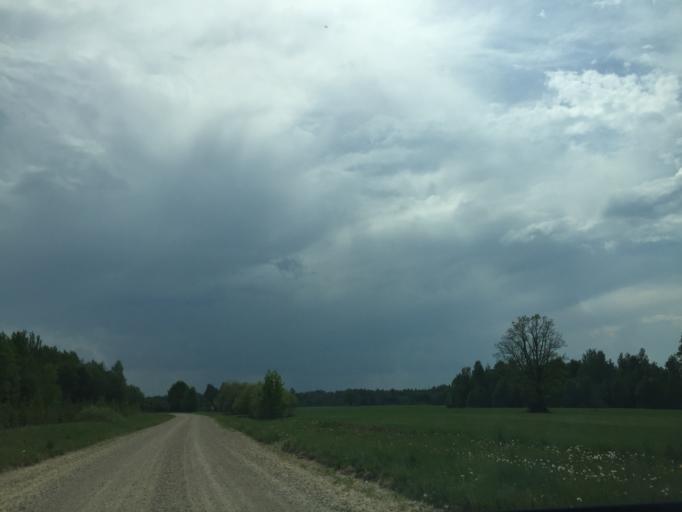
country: LV
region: Livani
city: Livani
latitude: 56.5740
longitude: 26.2164
